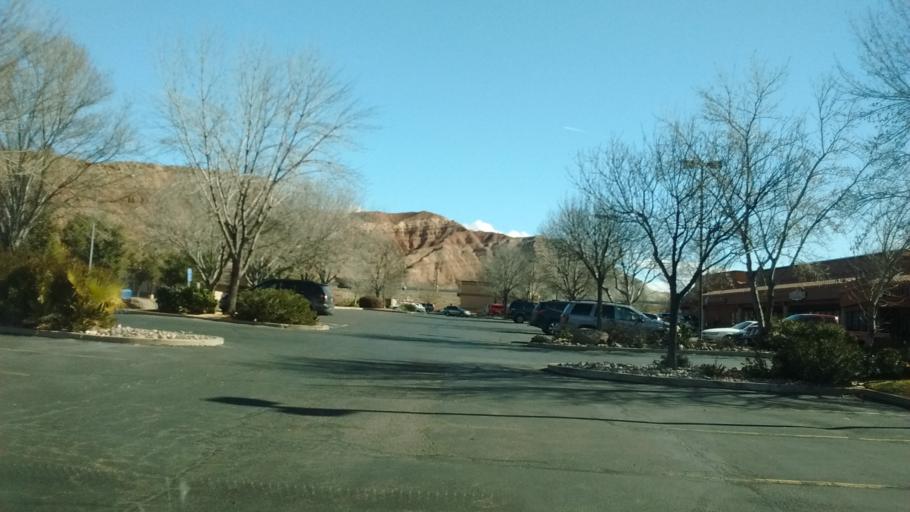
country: US
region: Utah
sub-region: Washington County
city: Saint George
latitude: 37.0617
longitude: -113.5869
